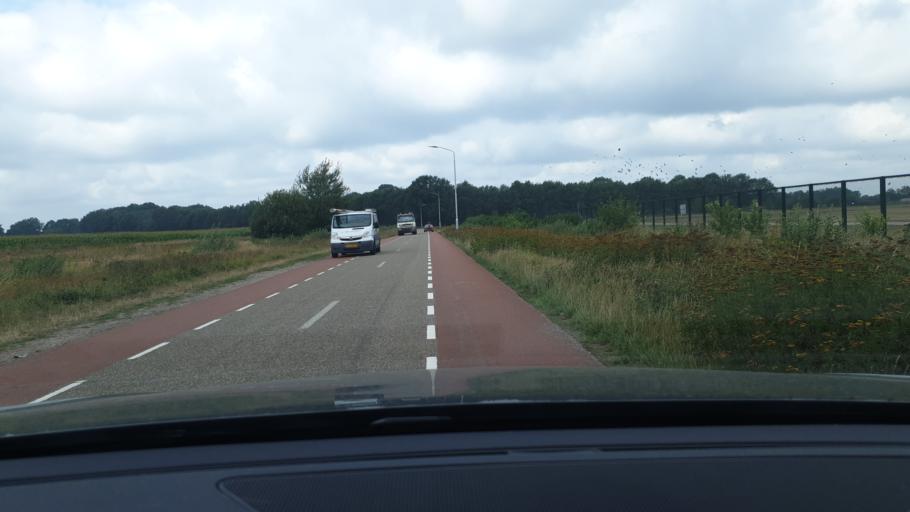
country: NL
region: North Brabant
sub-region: Gemeente Veldhoven
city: Oerle
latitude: 51.4371
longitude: 5.3600
